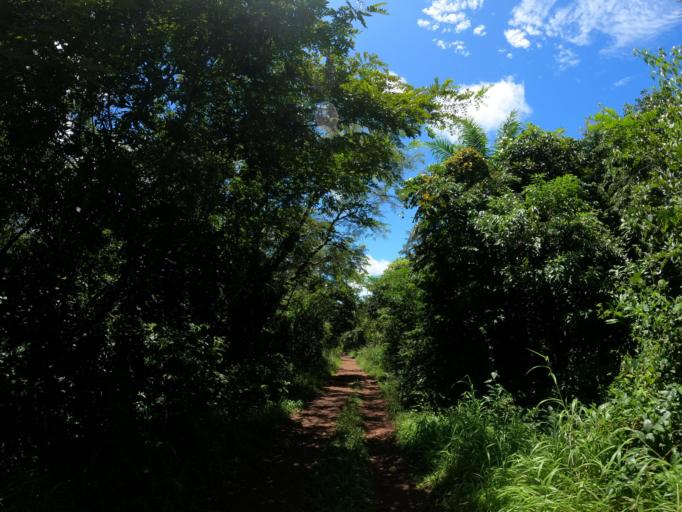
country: SL
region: Northern Province
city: Makeni
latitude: 9.0695
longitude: -12.2760
